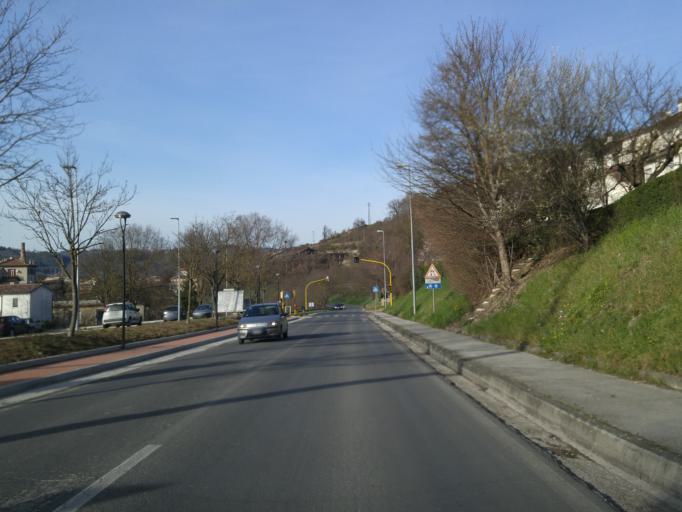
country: IT
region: The Marches
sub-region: Provincia di Pesaro e Urbino
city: Fermignano
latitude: 43.6740
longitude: 12.6479
